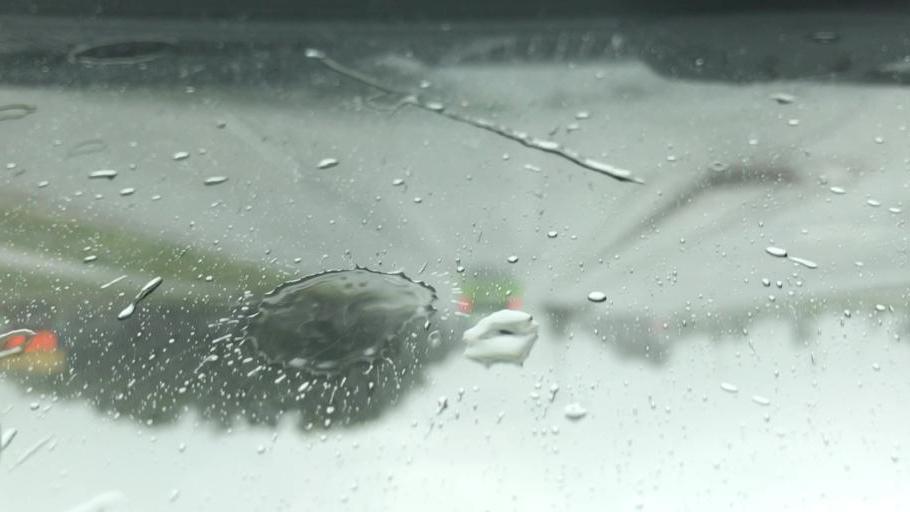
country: US
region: Texas
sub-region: Williamson County
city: Leander
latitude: 30.5421
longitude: -97.8632
